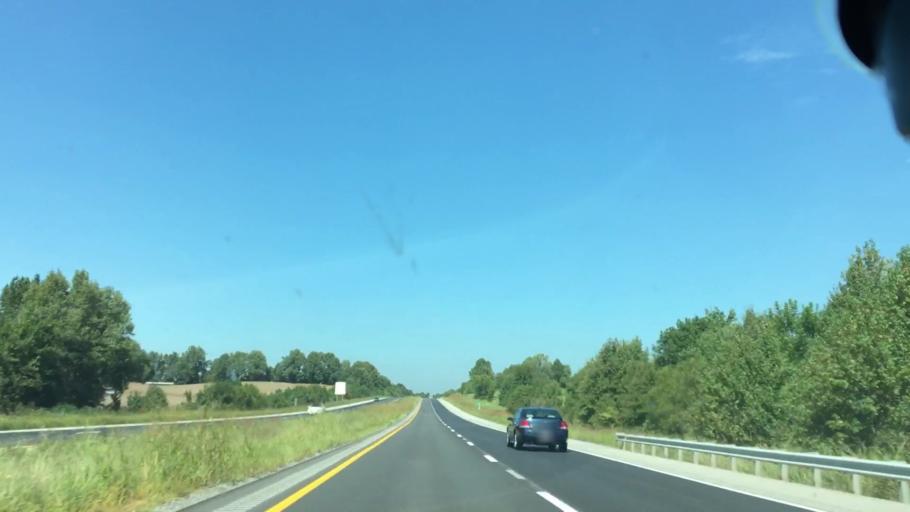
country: US
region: Kentucky
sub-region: Hopkins County
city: Madisonville
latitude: 37.4469
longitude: -87.4763
